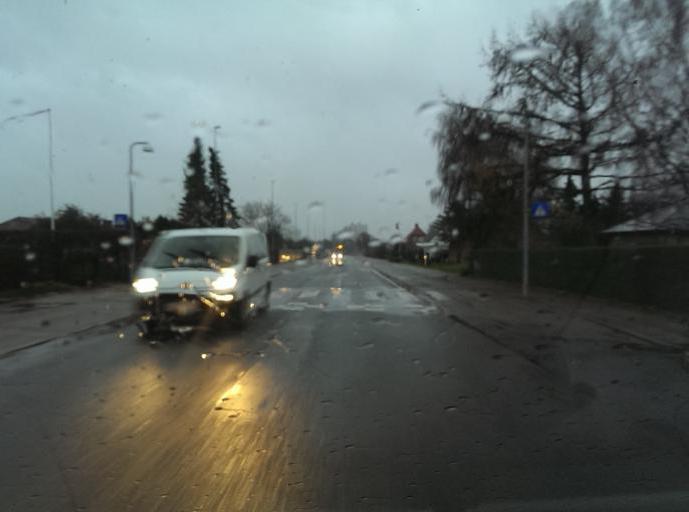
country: DK
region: South Denmark
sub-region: Esbjerg Kommune
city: Esbjerg
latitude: 55.5051
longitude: 8.4500
